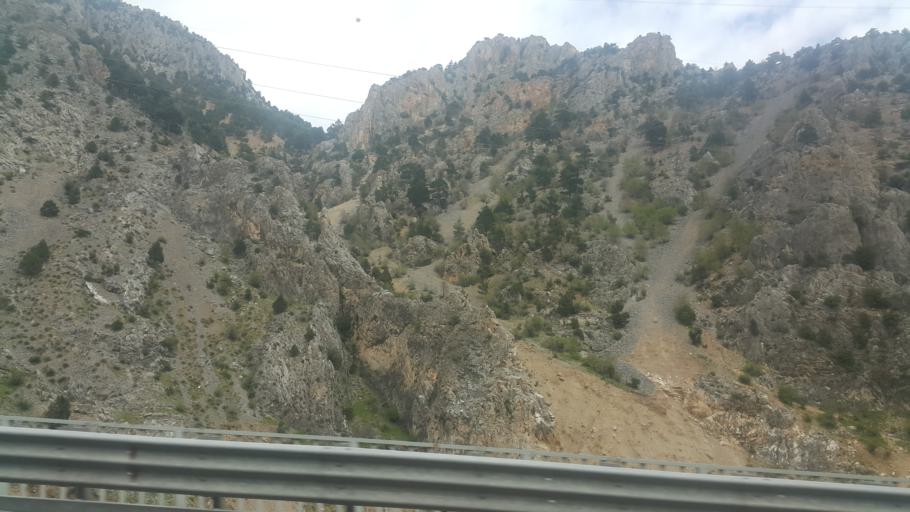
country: TR
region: Adana
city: Pozanti
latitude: 37.4731
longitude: 34.8618
